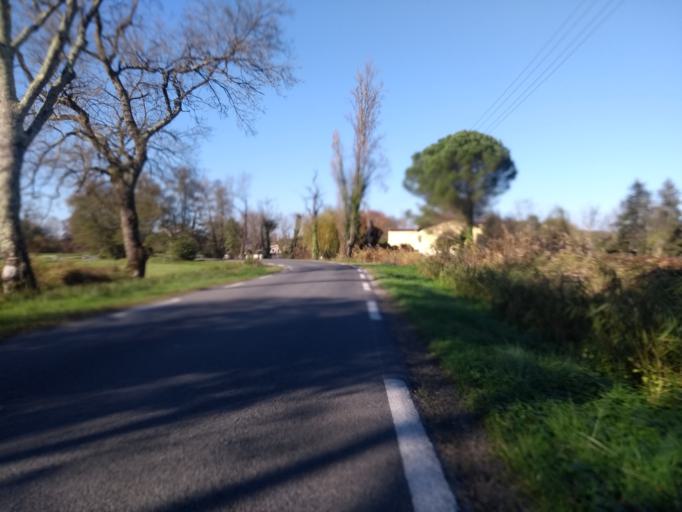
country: FR
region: Aquitaine
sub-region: Departement de la Gironde
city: Cambes
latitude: 44.7220
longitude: -0.4708
